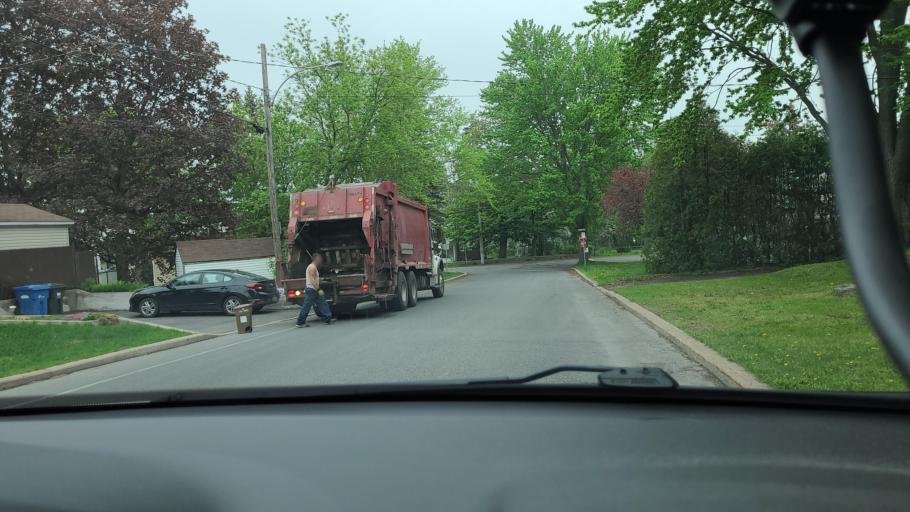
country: CA
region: Quebec
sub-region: Monteregie
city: L'Ile-Perrot
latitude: 45.3918
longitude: -73.9396
